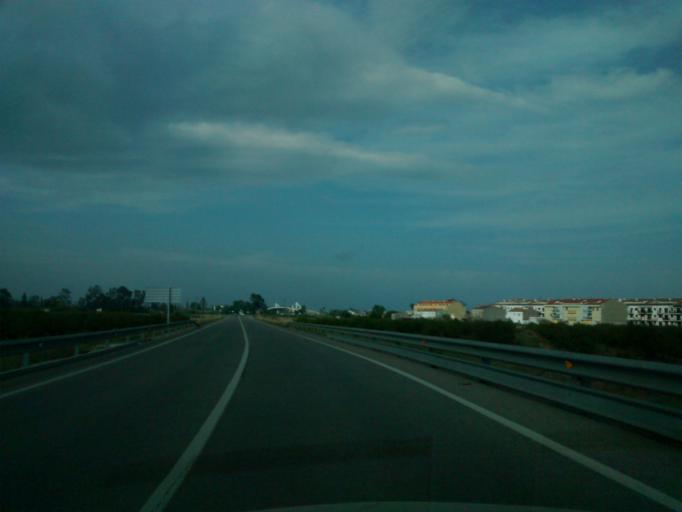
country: ES
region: Catalonia
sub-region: Provincia de Tarragona
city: Deltebre
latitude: 40.7061
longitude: 0.7117
